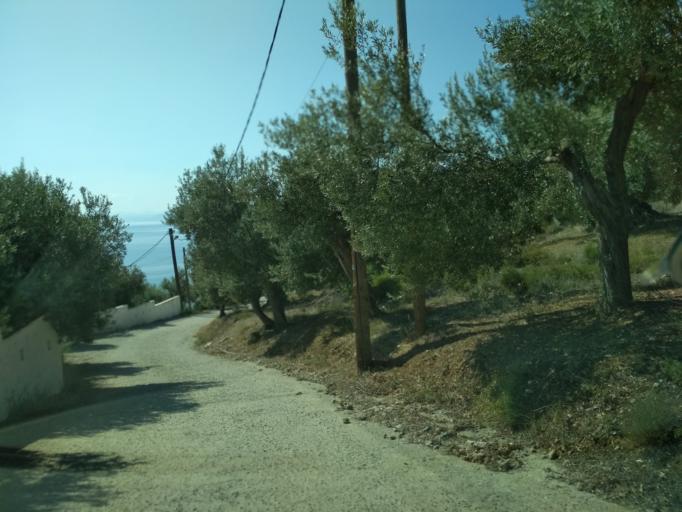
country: GR
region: Central Greece
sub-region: Nomos Evvoias
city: Oreoi
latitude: 38.8501
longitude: 23.1222
